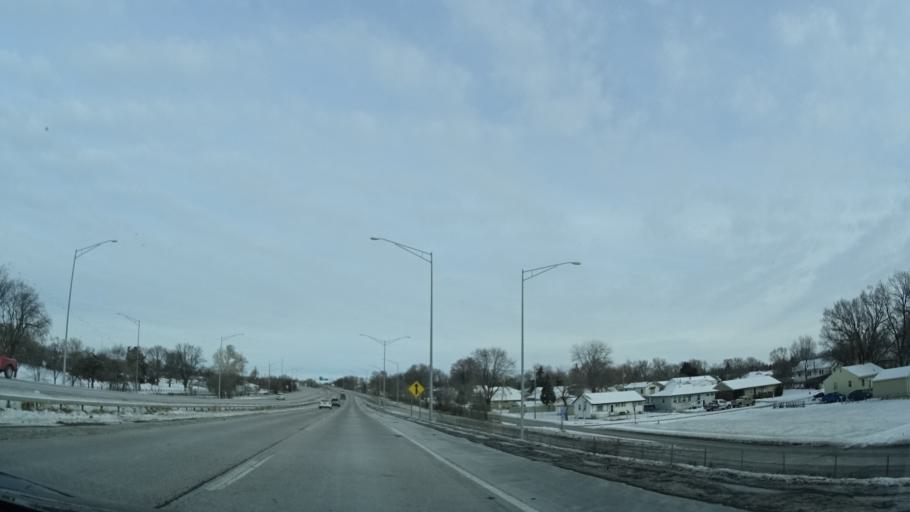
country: US
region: Nebraska
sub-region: Douglas County
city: Omaha
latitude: 41.2546
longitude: -95.9067
